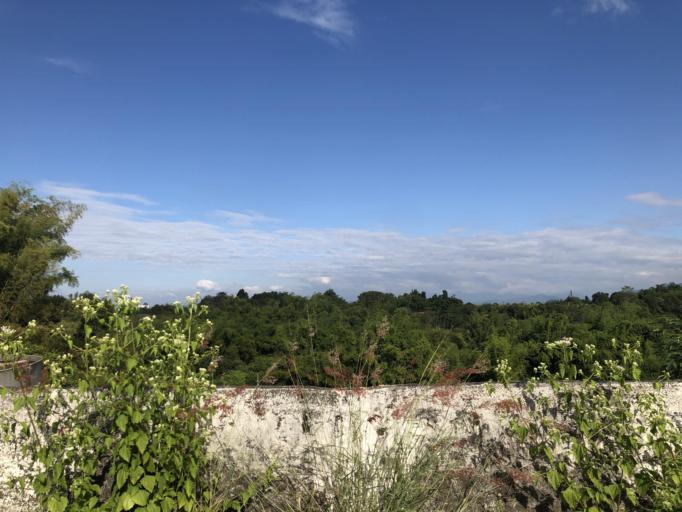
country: TW
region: Taiwan
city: Yujing
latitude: 23.0510
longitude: 120.4015
